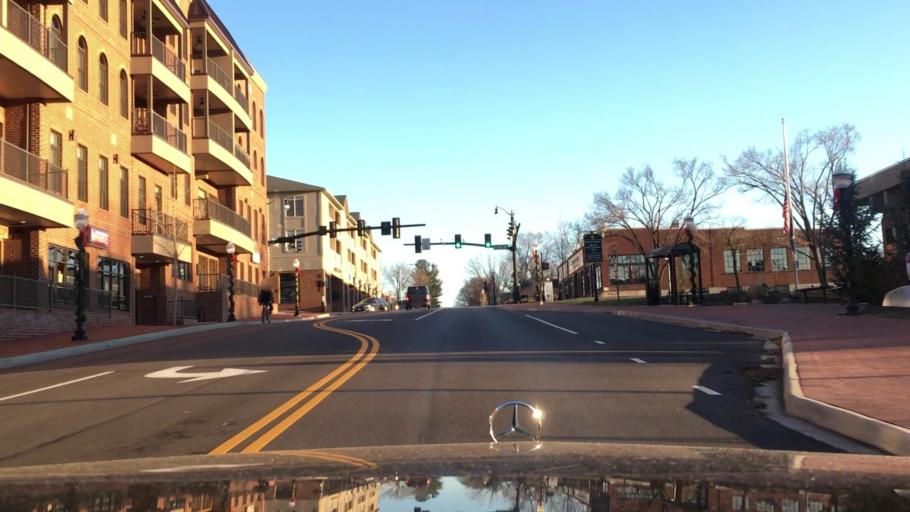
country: US
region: Virginia
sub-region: Montgomery County
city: Blacksburg
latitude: 37.2277
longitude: -80.4123
